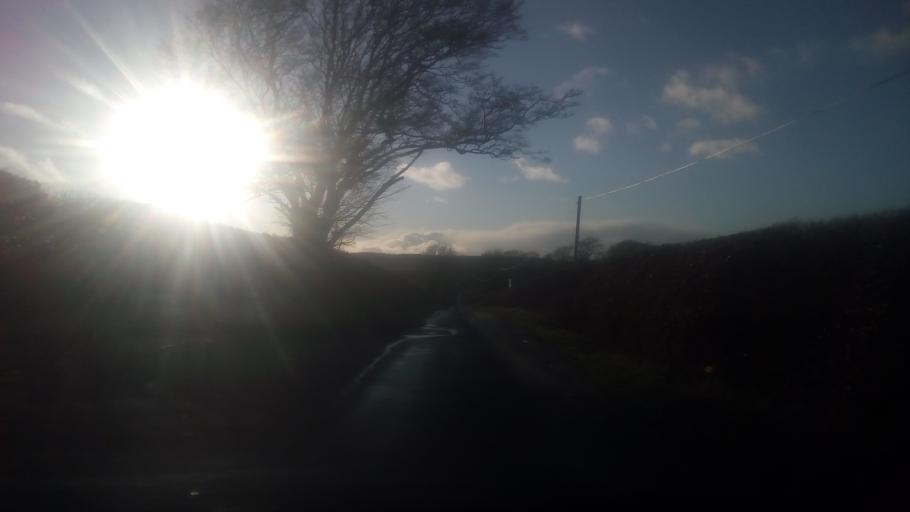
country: GB
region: Scotland
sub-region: The Scottish Borders
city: Jedburgh
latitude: 55.4703
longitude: -2.4678
